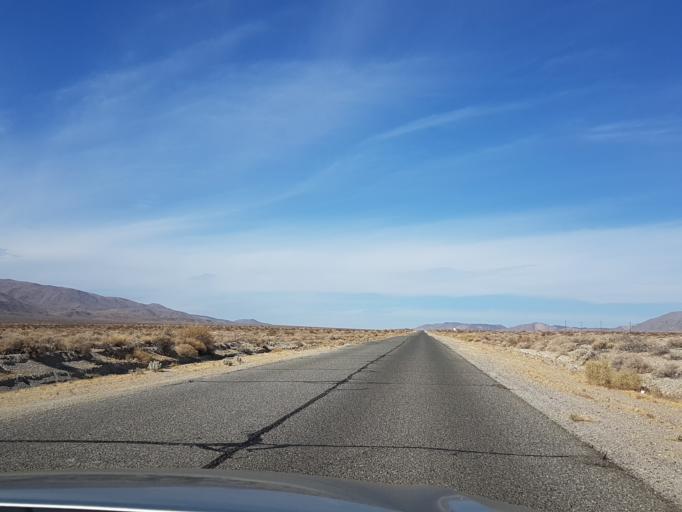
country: US
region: California
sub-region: San Bernardino County
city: Searles Valley
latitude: 35.8413
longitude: -117.3367
